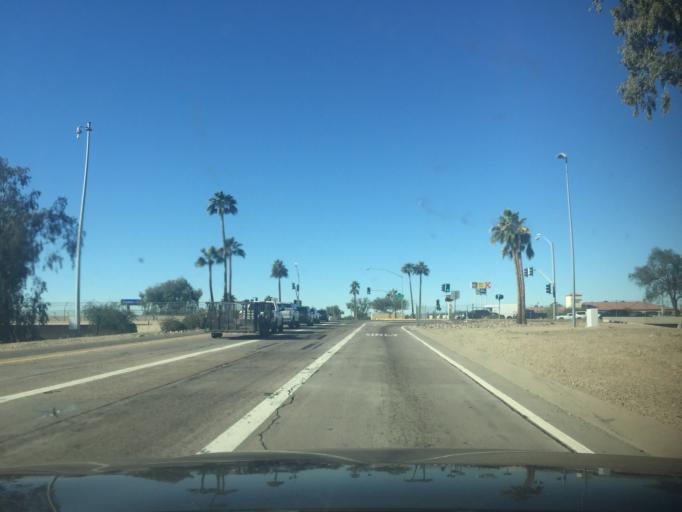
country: US
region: Arizona
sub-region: Maricopa County
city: Tolleson
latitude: 33.4629
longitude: -112.2372
